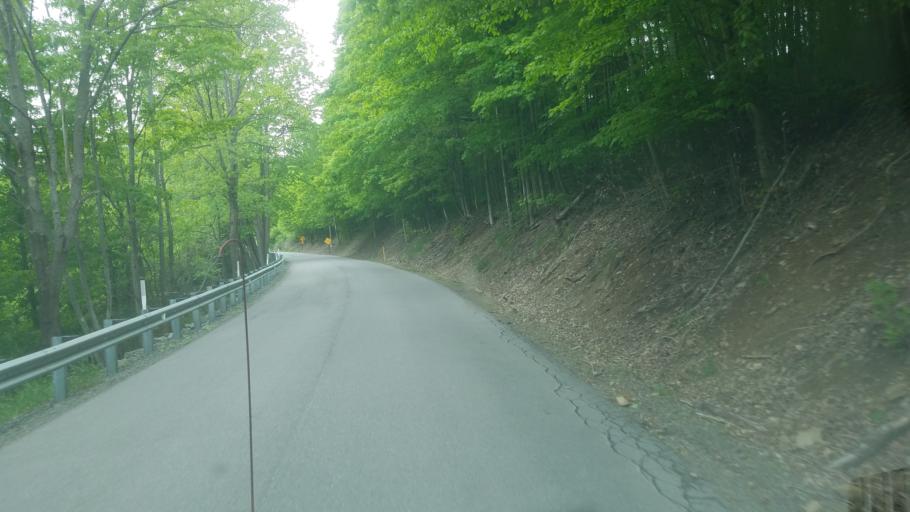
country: US
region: Pennsylvania
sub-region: Tioga County
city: Westfield
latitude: 41.8321
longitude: -77.5893
